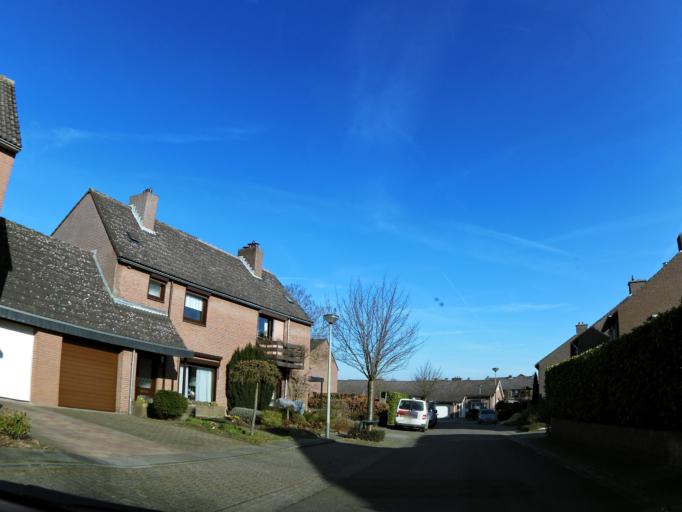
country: NL
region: Limburg
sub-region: Gemeente Kerkrade
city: Kerkrade
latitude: 50.9213
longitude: 6.0342
